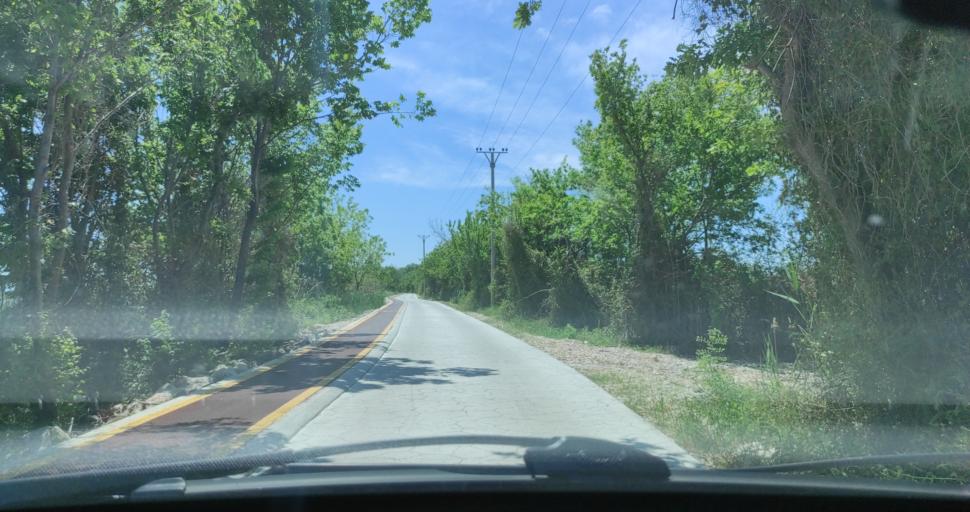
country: AL
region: Lezhe
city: Shengjin
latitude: 41.7431
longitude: 19.5822
